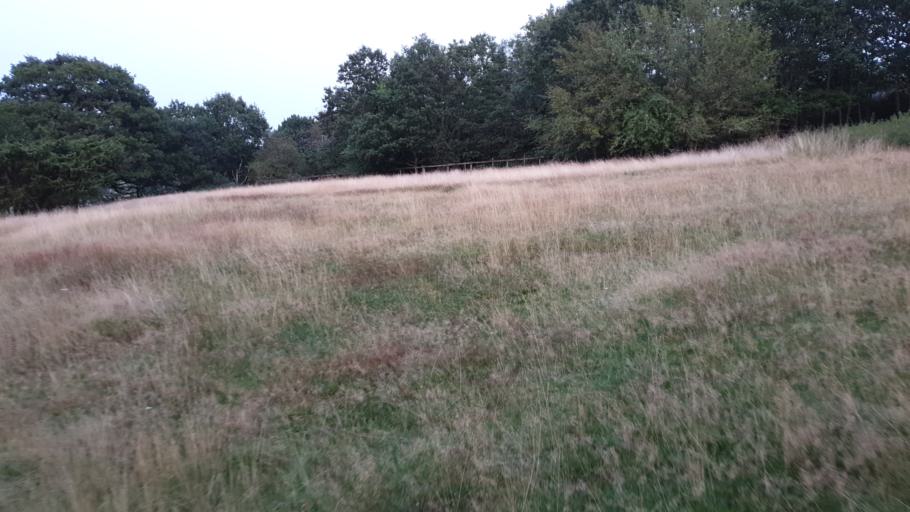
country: SE
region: Vaestra Goetaland
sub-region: Goteborg
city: Billdal
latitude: 57.5919
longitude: 11.9155
